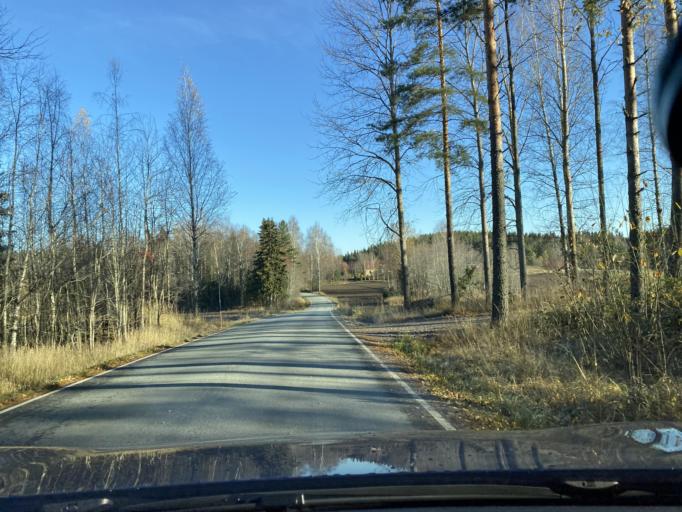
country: FI
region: Haeme
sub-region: Haemeenlinna
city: Kalvola
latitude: 61.0112
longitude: 24.1307
